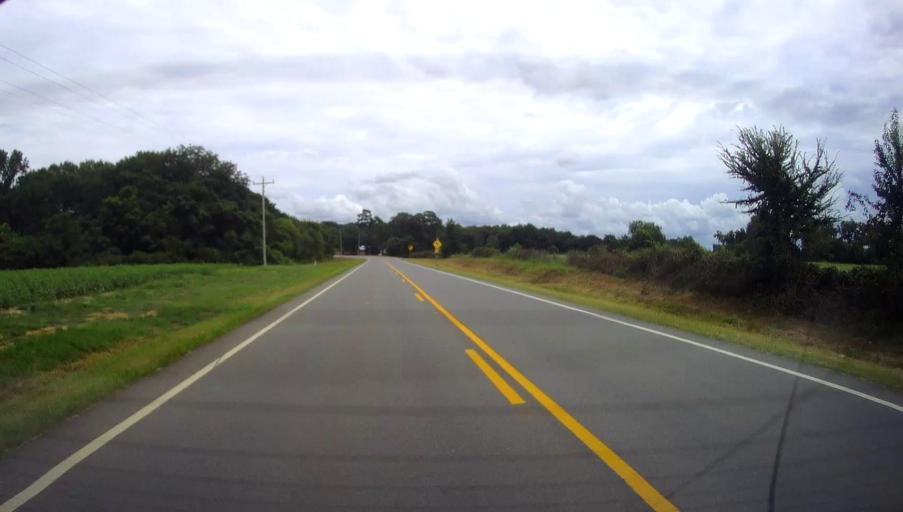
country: US
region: Georgia
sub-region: Macon County
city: Montezuma
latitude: 32.2914
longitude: -83.9221
